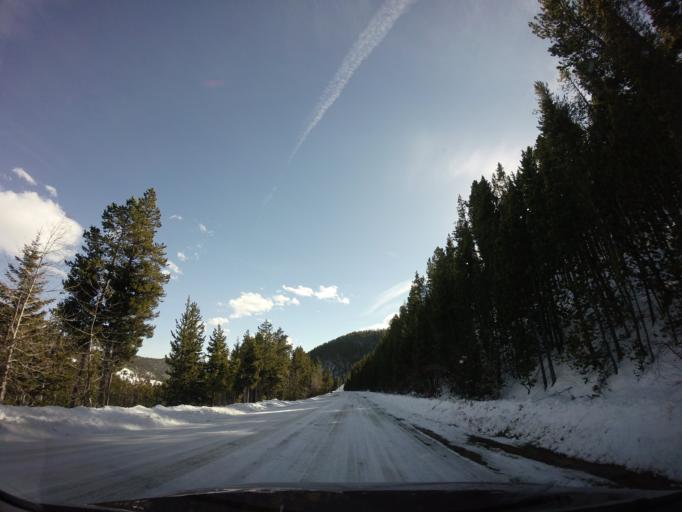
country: US
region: Montana
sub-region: Carbon County
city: Red Lodge
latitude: 45.1880
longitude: -109.3324
